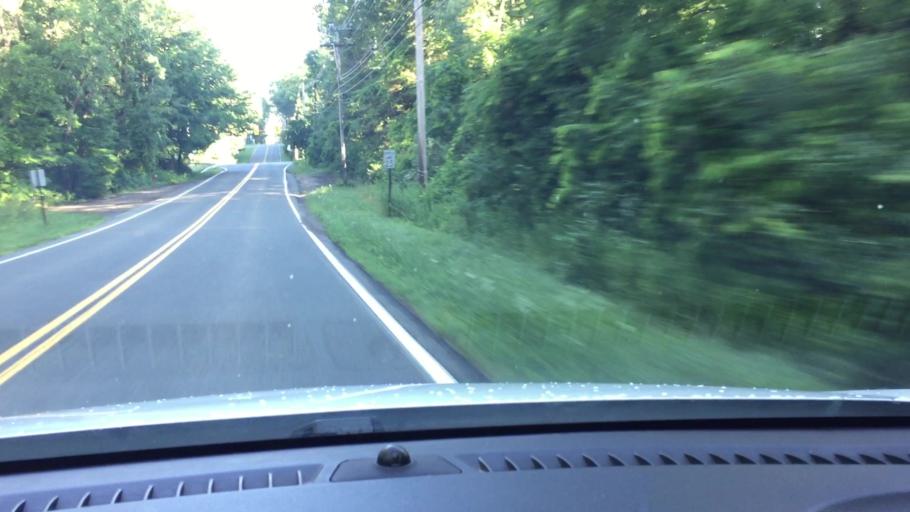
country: US
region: Massachusetts
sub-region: Berkshire County
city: Lenox
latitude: 42.3468
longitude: -73.2677
